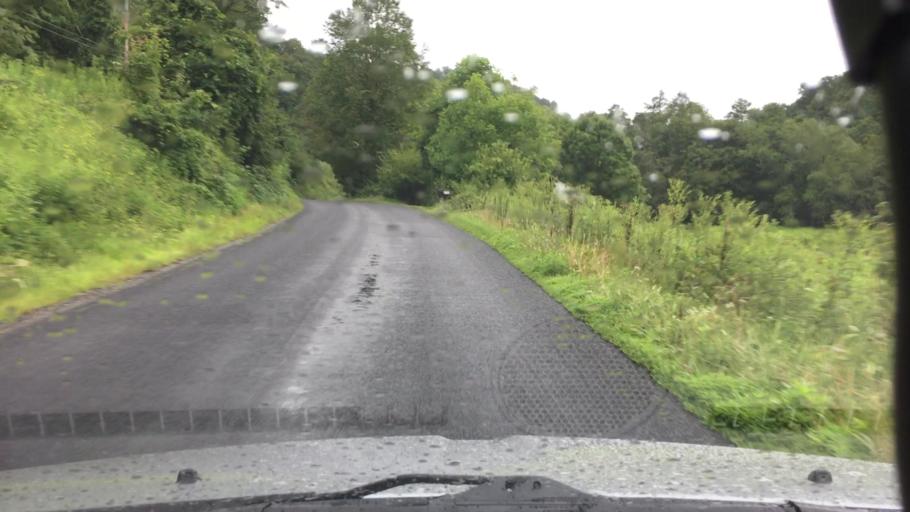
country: US
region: North Carolina
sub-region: Madison County
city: Mars Hill
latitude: 35.9118
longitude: -82.5094
